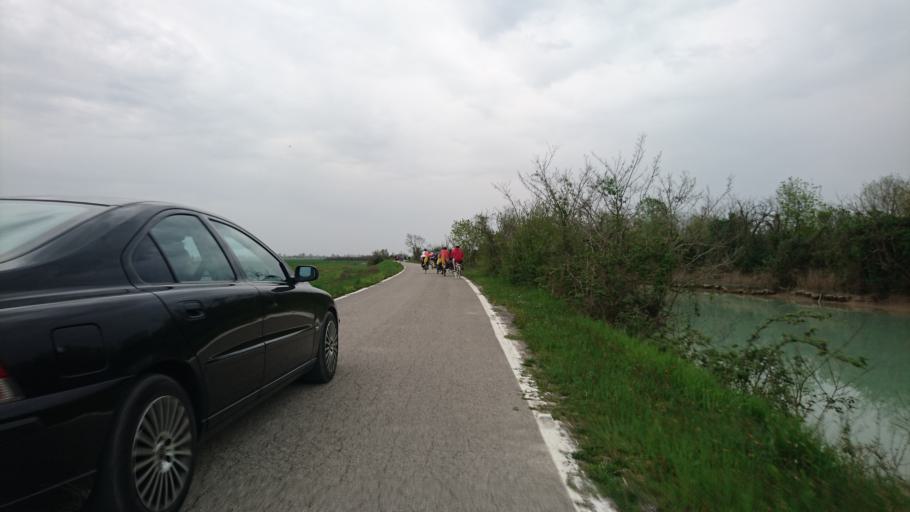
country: IT
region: Veneto
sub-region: Provincia di Venezia
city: Bibione
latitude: 45.6537
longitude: 13.0293
